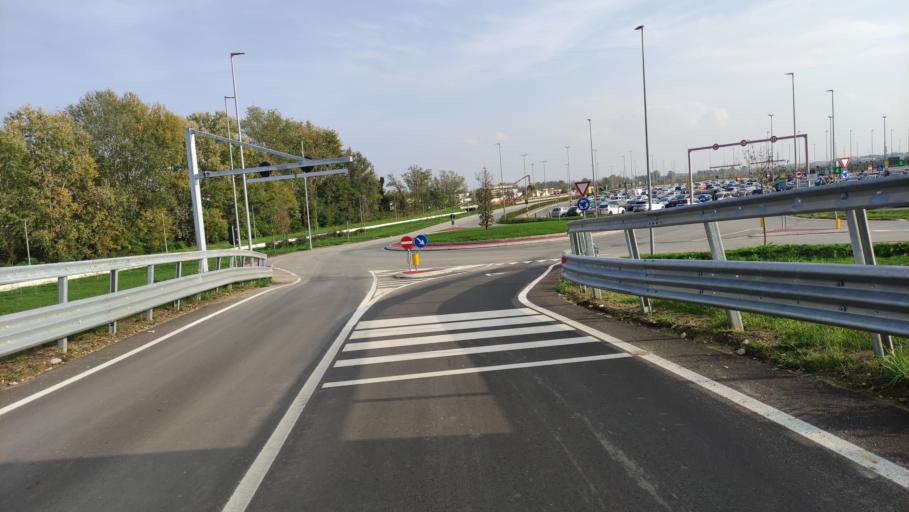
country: IT
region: Piedmont
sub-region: Provincia di Novara
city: San Pietro Mosezzo
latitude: 45.4741
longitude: 8.5767
